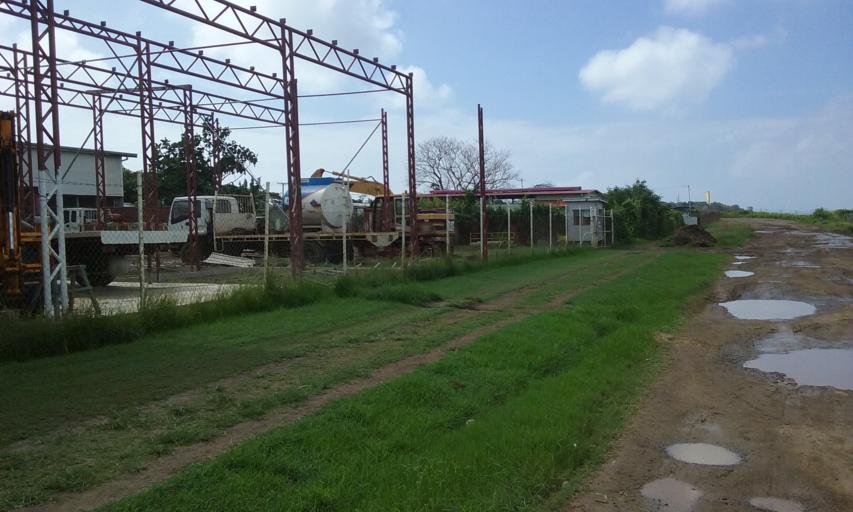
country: PG
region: Western Province
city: Daru
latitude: -9.0819
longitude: 143.2042
